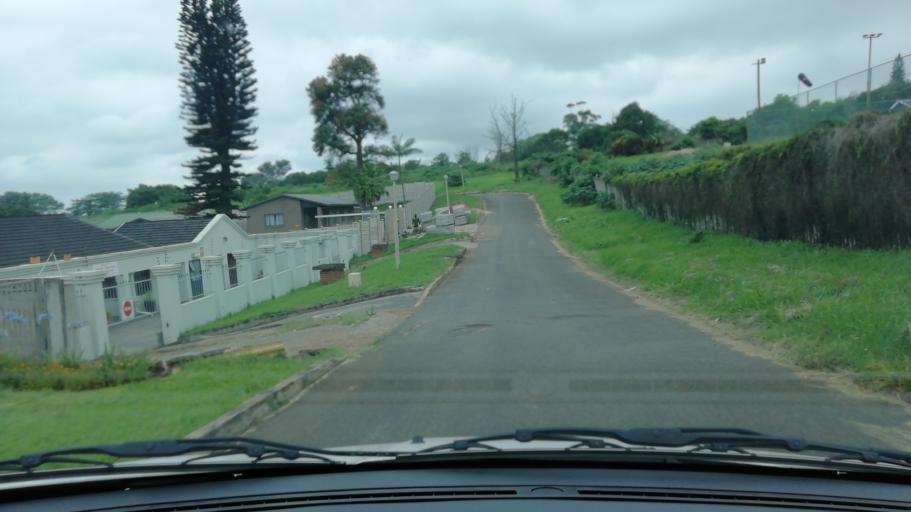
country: ZA
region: KwaZulu-Natal
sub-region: uThungulu District Municipality
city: Empangeni
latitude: -28.7439
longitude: 31.8941
